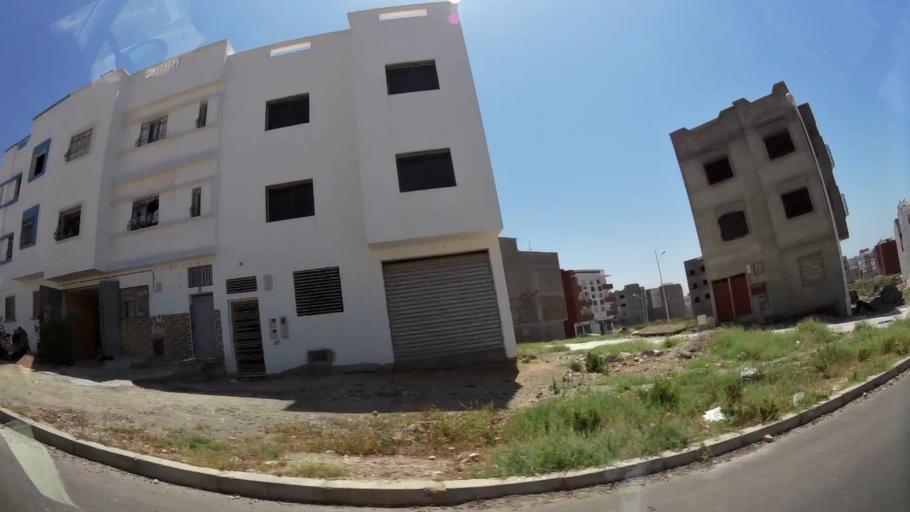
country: MA
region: Oued ed Dahab-Lagouira
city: Dakhla
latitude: 30.4449
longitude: -9.5600
